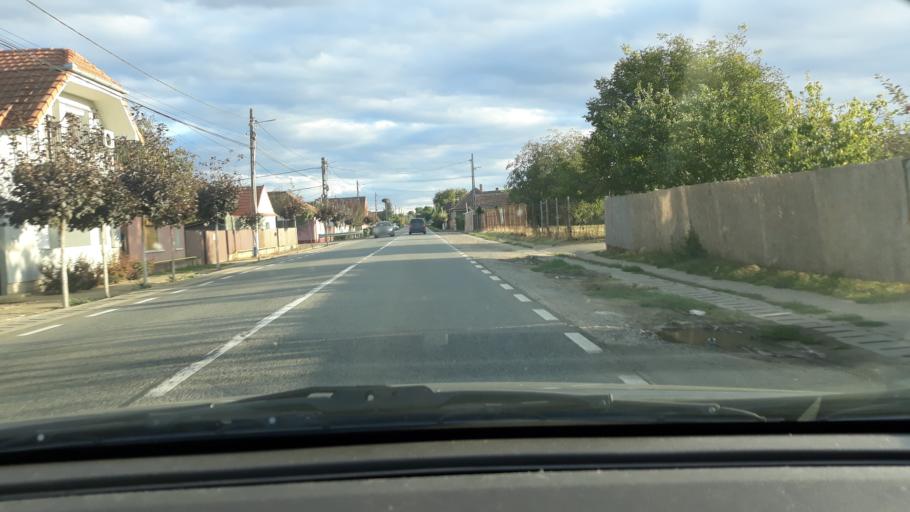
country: RO
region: Bihor
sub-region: Comuna Biharea
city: Biharea
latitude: 47.1665
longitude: 21.9220
